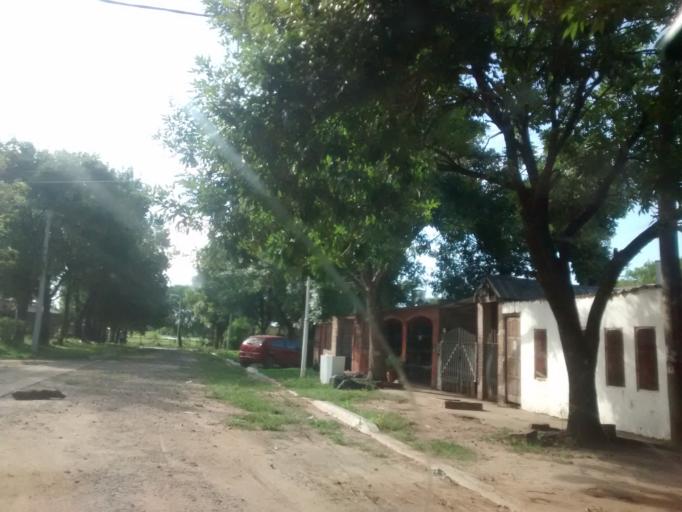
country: AR
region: Chaco
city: Puerto Tirol
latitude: -27.3753
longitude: -59.0925
